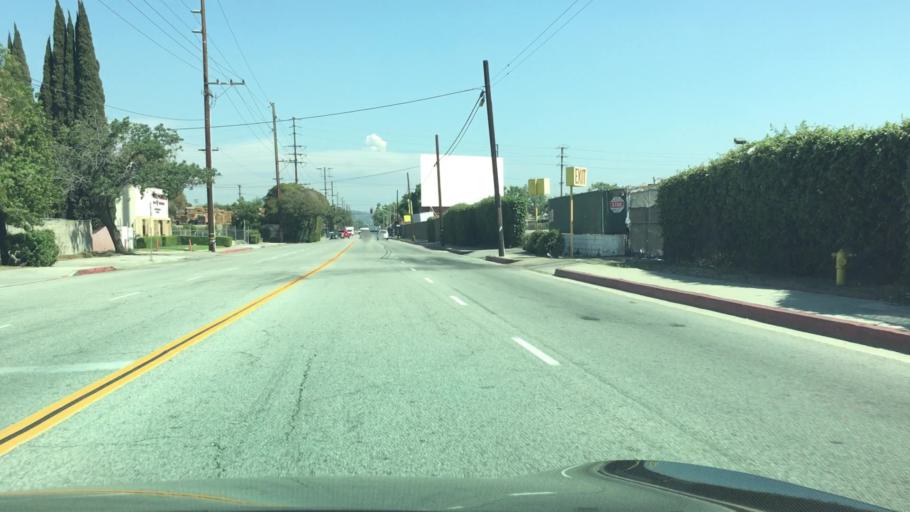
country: US
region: California
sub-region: Los Angeles County
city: Avocado Heights
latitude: 34.0551
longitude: -117.9886
